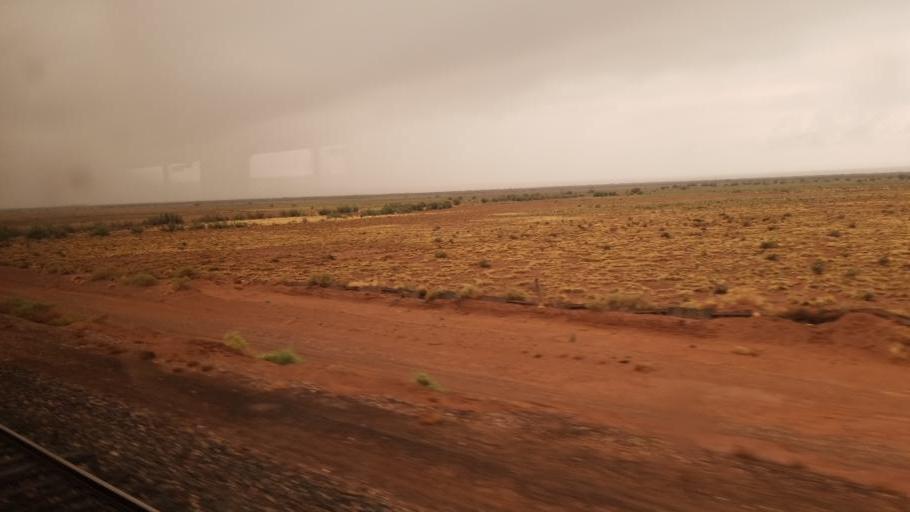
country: US
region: Arizona
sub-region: Navajo County
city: Joseph City
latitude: 34.9676
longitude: -110.5072
